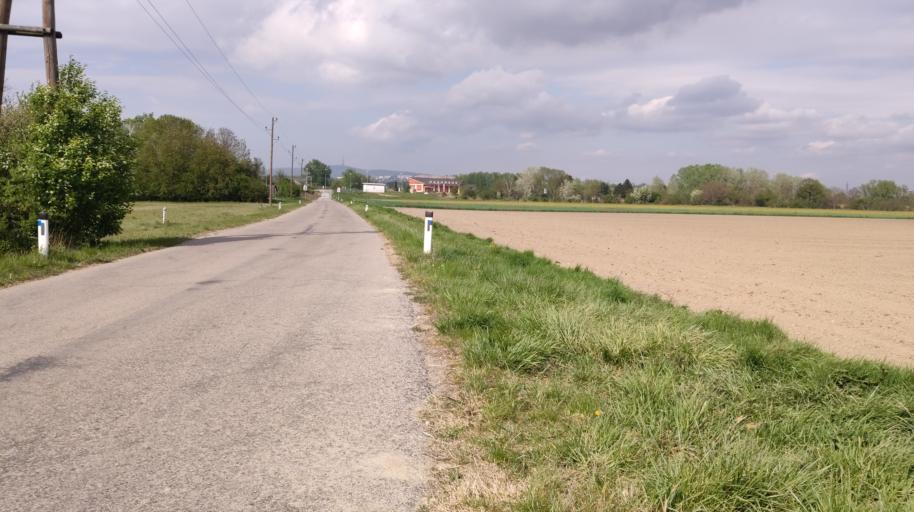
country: AT
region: Burgenland
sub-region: Politischer Bezirk Neusiedl am See
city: Kittsee
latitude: 48.1190
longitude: 17.0601
